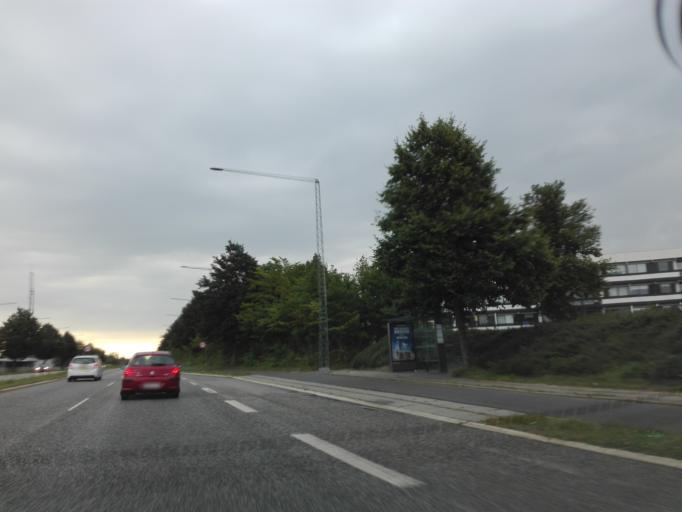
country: DK
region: Central Jutland
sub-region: Arhus Kommune
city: Lystrup
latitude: 56.2058
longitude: 10.2632
